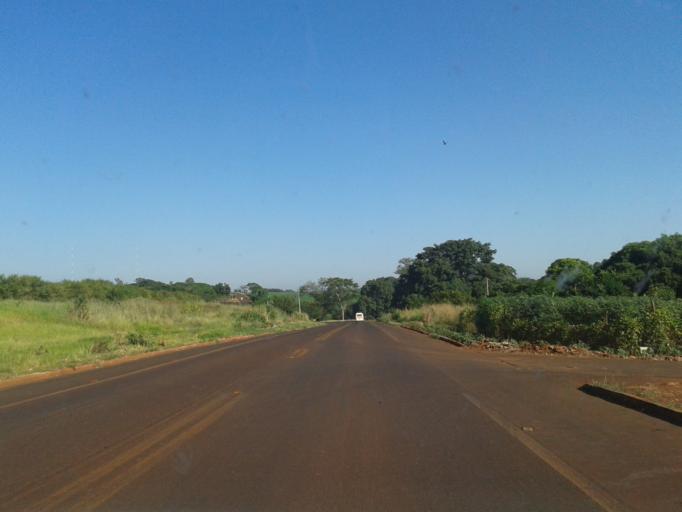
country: BR
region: Minas Gerais
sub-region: Capinopolis
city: Capinopolis
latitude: -18.6858
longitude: -49.5831
